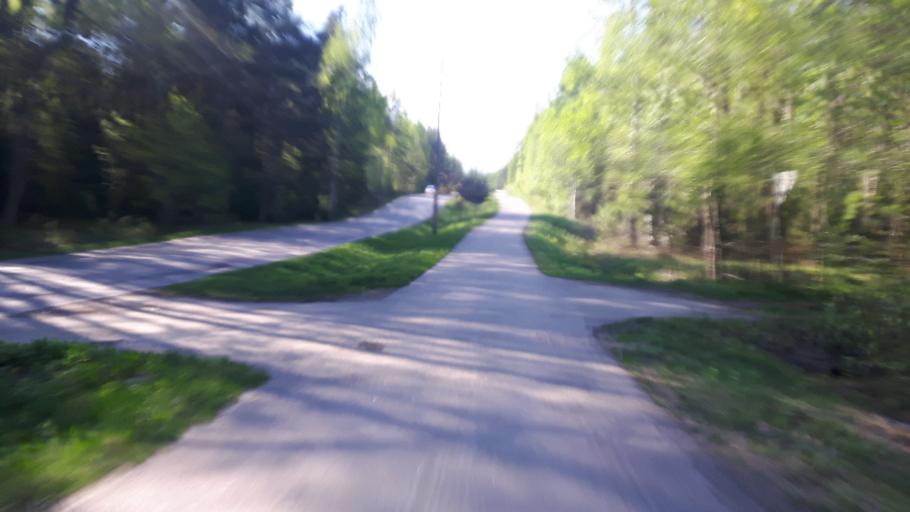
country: FI
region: Kymenlaakso
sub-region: Kotka-Hamina
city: Kotka
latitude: 60.4368
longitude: 26.8751
